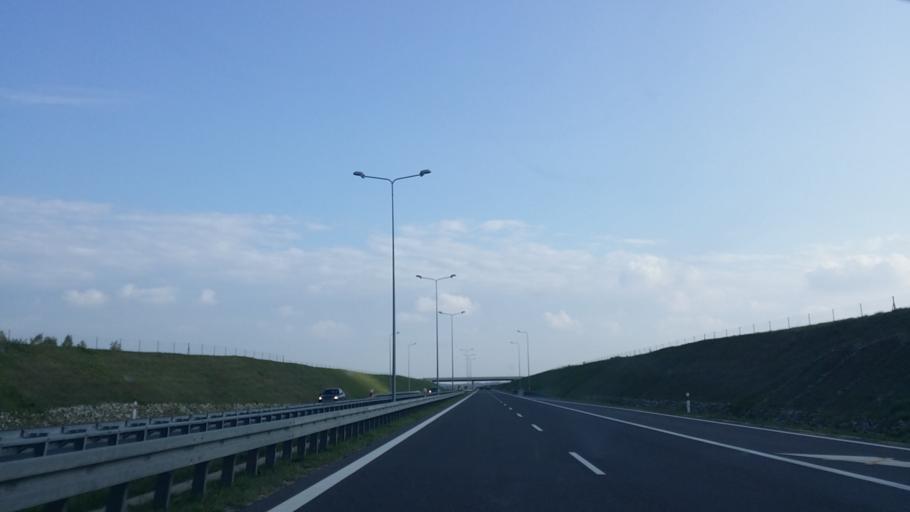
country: PL
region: Lubusz
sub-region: Powiat miedzyrzecki
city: Miedzyrzecz
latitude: 52.3789
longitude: 15.5461
